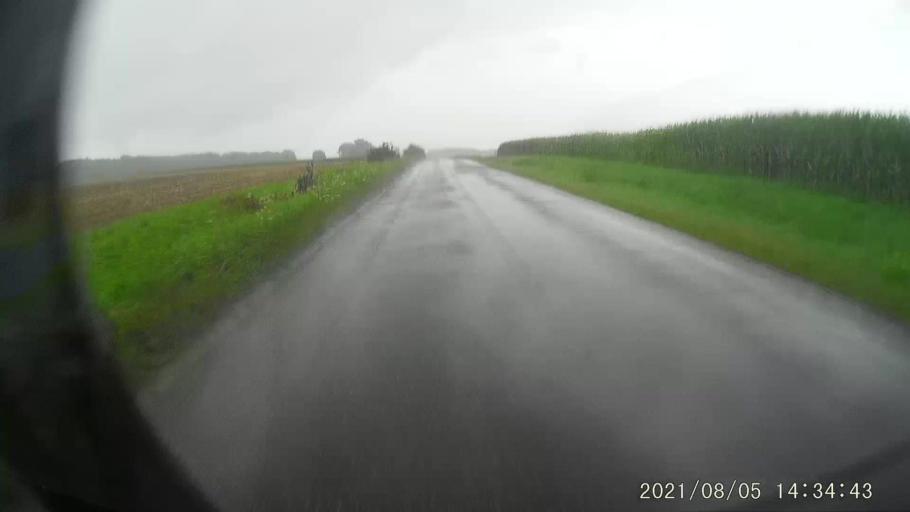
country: PL
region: Opole Voivodeship
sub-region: Powiat nyski
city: Lambinowice
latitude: 50.4674
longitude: 17.5145
